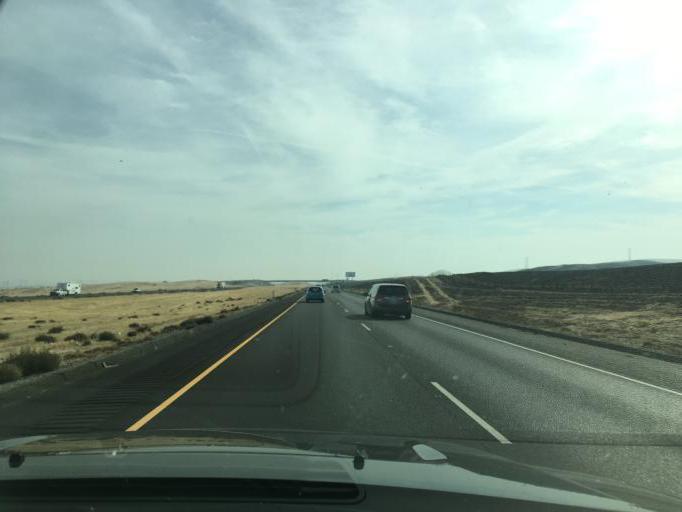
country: US
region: California
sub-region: Kings County
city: Kettleman City
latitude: 36.0137
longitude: -119.9970
